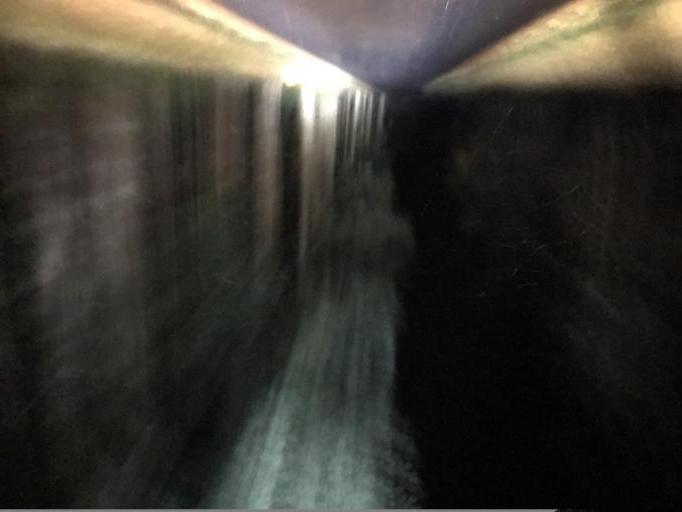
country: FR
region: Auvergne
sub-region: Departement du Puy-de-Dome
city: Celles-sur-Durolle
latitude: 45.8948
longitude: 3.6374
